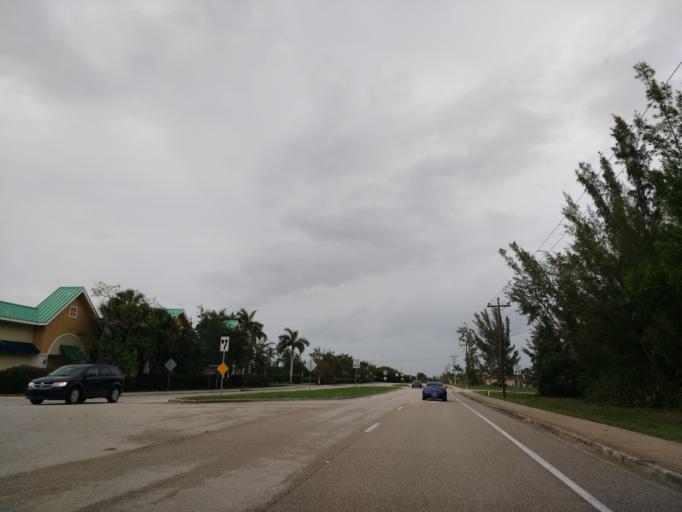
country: US
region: Florida
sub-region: Lee County
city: Cape Coral
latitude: 26.6086
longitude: -82.0233
